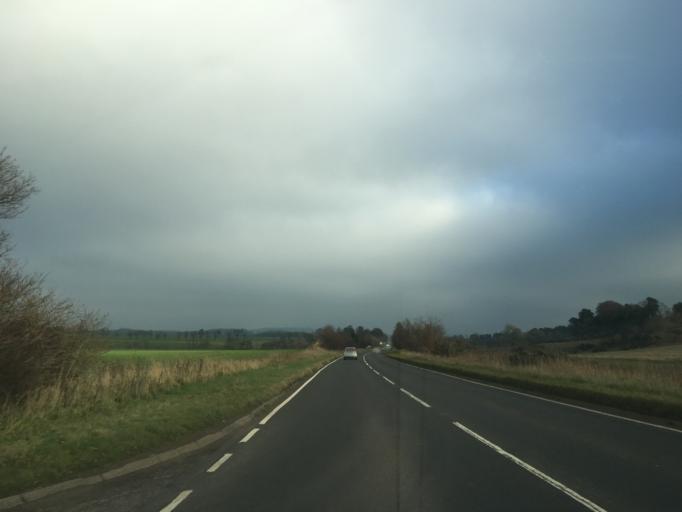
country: GB
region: Scotland
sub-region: Perth and Kinross
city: Milnathort
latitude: 56.2536
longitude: -3.3582
